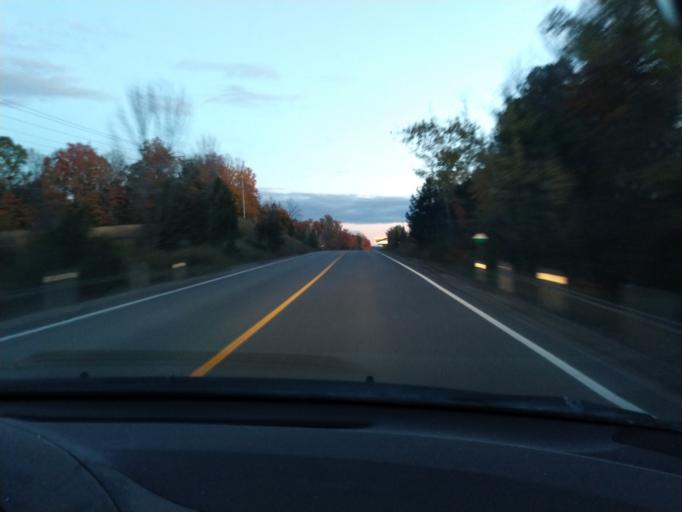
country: CA
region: Ontario
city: Innisfil
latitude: 44.2044
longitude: -79.6662
